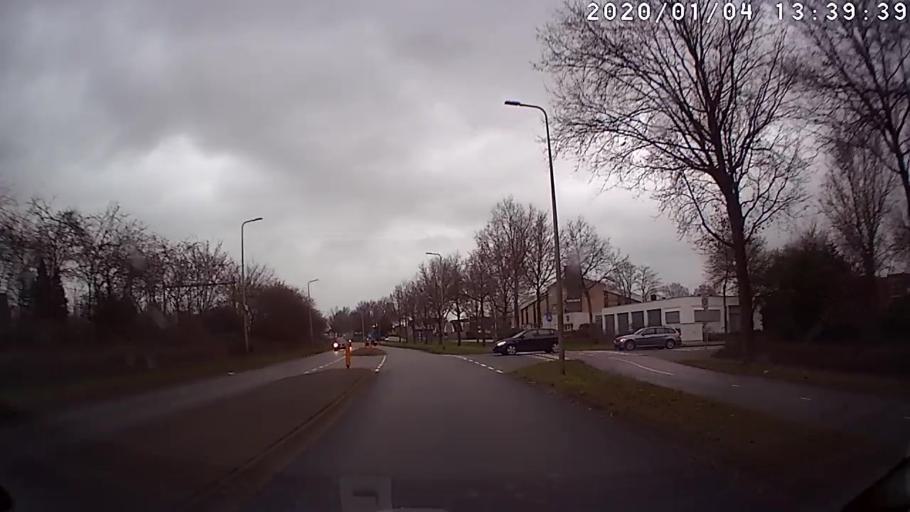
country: NL
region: Overijssel
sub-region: Gemeente Zwolle
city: Zwolle
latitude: 52.4889
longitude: 6.1044
